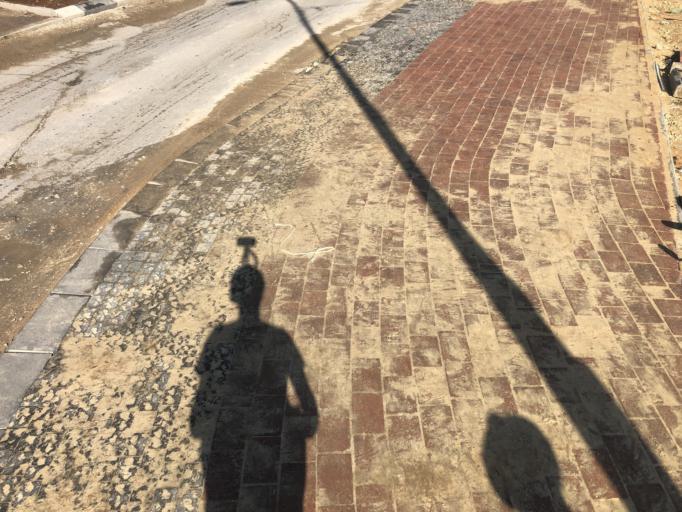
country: IL
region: Jerusalem
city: Modiin Ilit
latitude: 31.9248
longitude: 35.0463
